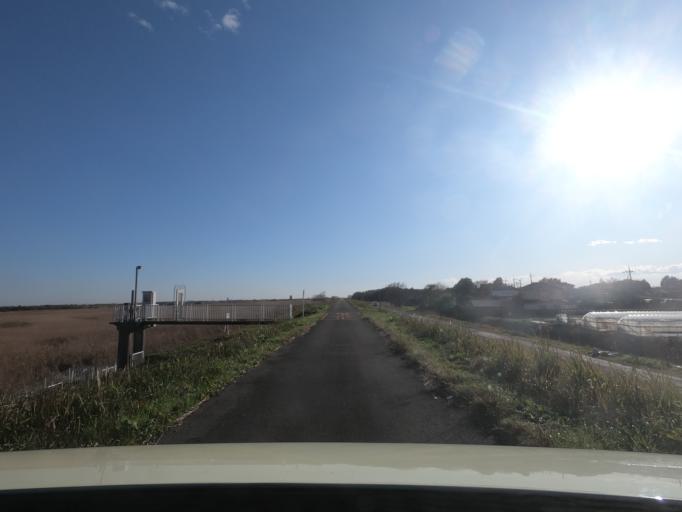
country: JP
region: Tochigi
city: Fujioka
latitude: 36.2711
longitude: 139.6801
